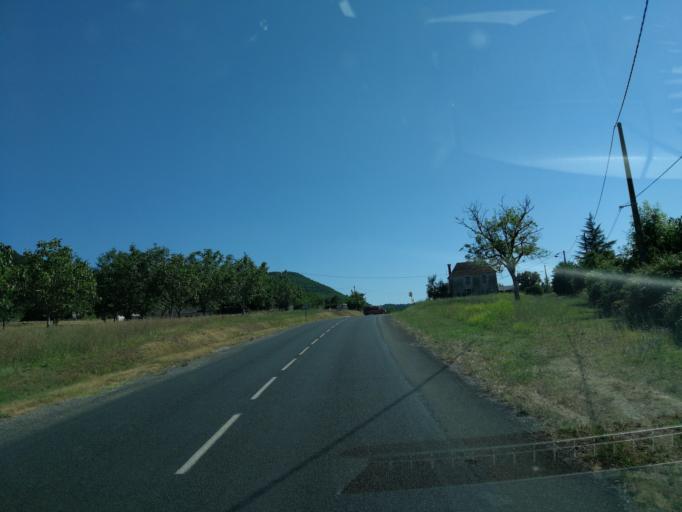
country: FR
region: Midi-Pyrenees
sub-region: Departement du Lot
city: Souillac
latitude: 44.8879
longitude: 1.4530
